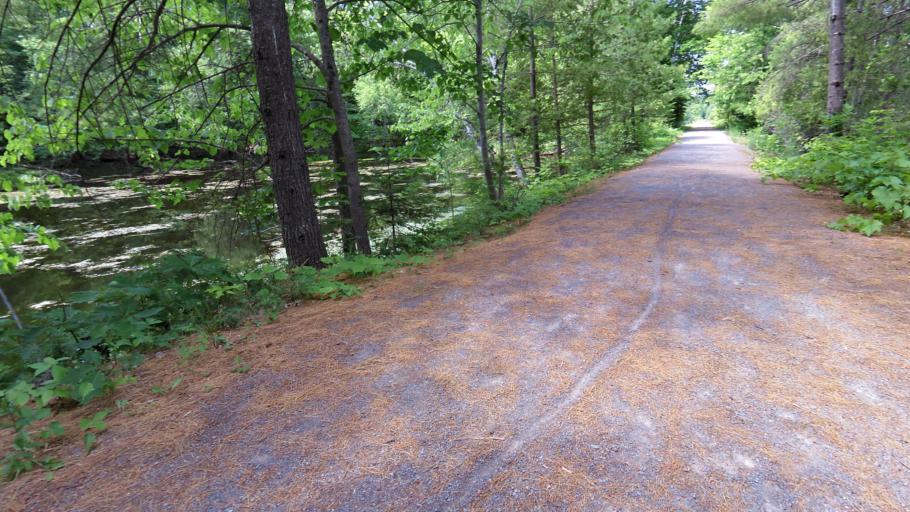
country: CA
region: Ontario
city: Arnprior
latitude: 45.4596
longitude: -76.2615
